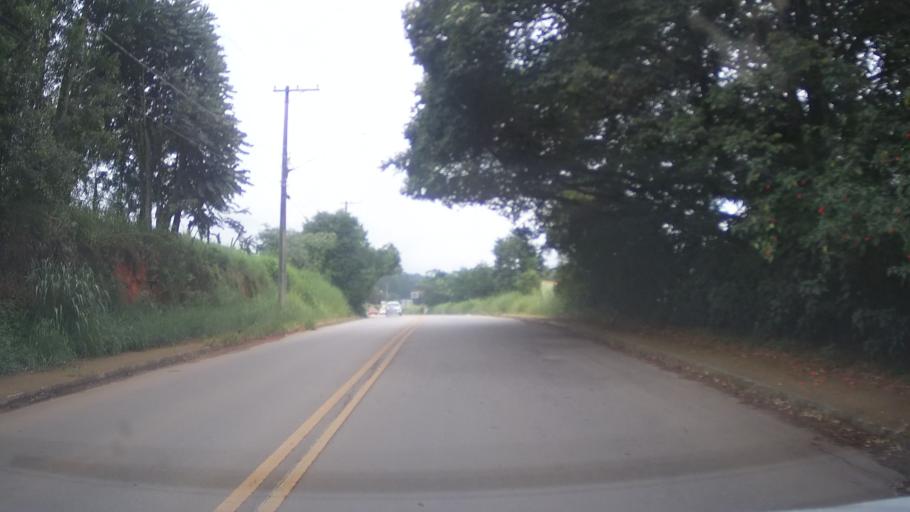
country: BR
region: Sao Paulo
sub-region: Varzea Paulista
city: Varzea Paulista
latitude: -23.1742
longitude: -46.8139
